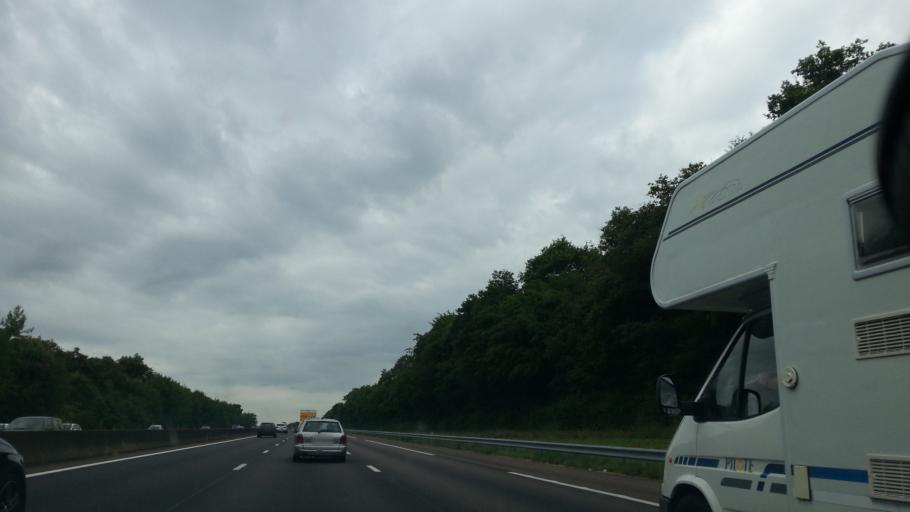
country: FR
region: Bourgogne
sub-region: Departement de Saone-et-Loire
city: Demigny
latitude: 46.8902
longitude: 4.8210
